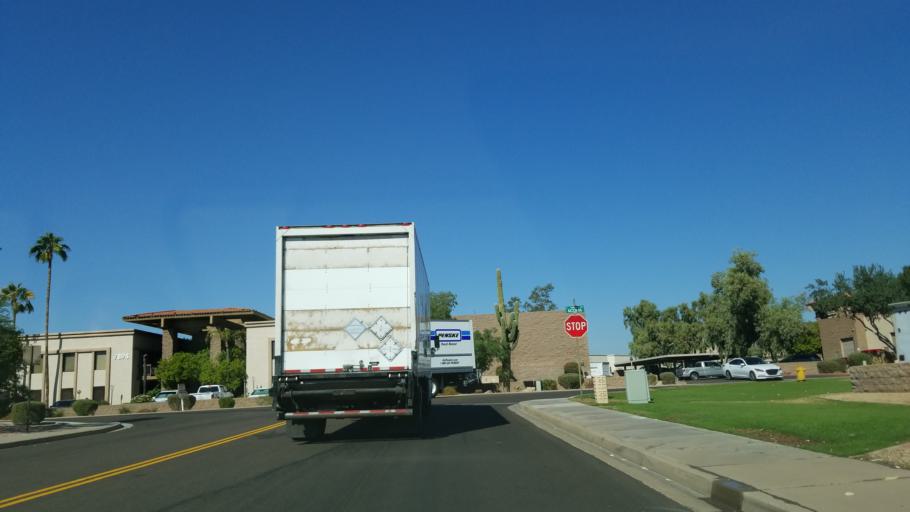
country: US
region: Arizona
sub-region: Maricopa County
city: Paradise Valley
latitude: 33.6174
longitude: -111.9099
